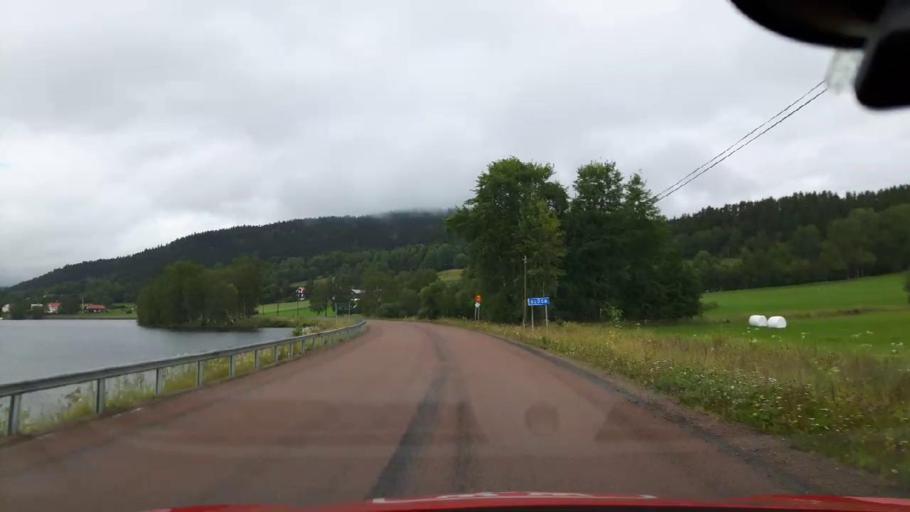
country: SE
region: Jaemtland
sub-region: Krokoms Kommun
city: Valla
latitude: 63.3788
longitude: 14.0149
